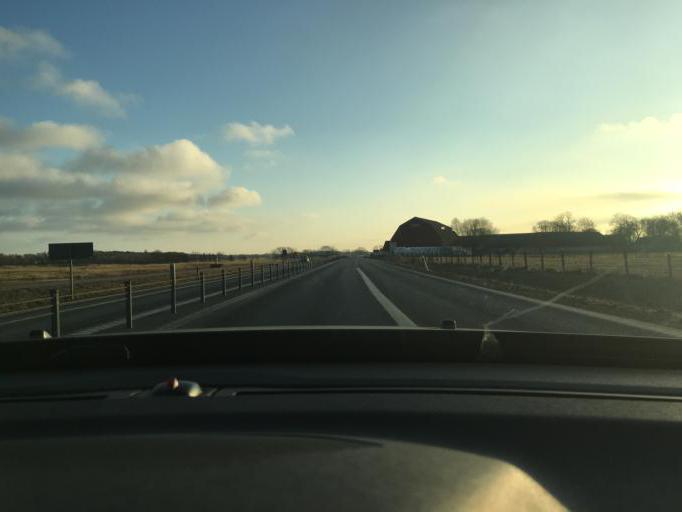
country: SE
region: Halland
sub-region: Varbergs Kommun
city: Varberg
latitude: 57.1446
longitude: 12.2677
